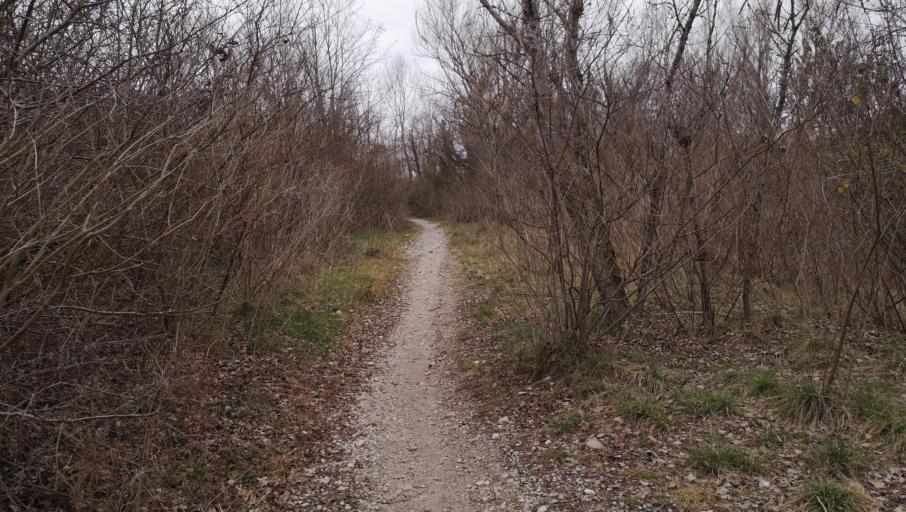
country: IT
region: Friuli Venezia Giulia
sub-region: Provincia di Udine
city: Povoletto
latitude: 46.1100
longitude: 13.2763
